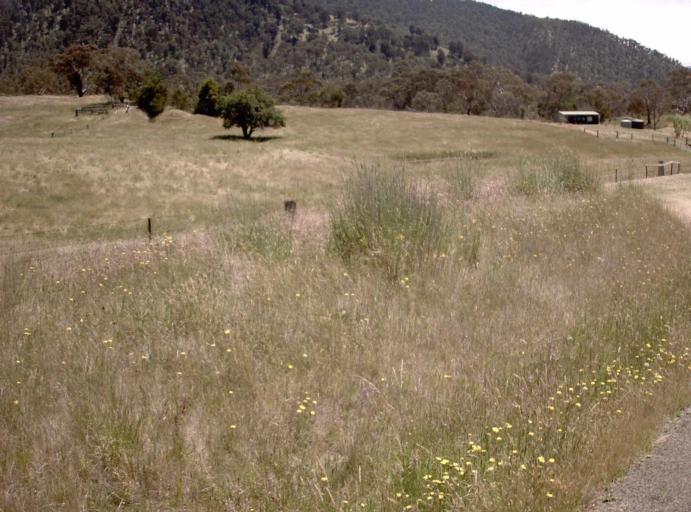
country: AU
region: Victoria
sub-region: Alpine
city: Mount Beauty
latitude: -37.1137
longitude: 147.5720
